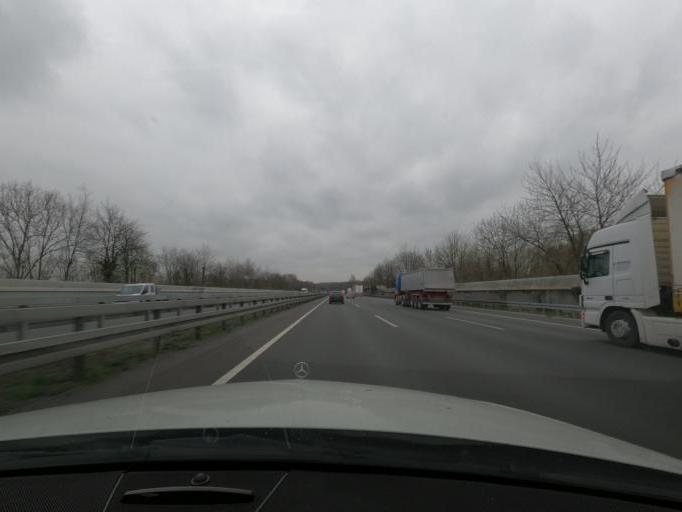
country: DE
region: North Rhine-Westphalia
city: Lunen
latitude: 51.5791
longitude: 7.5117
